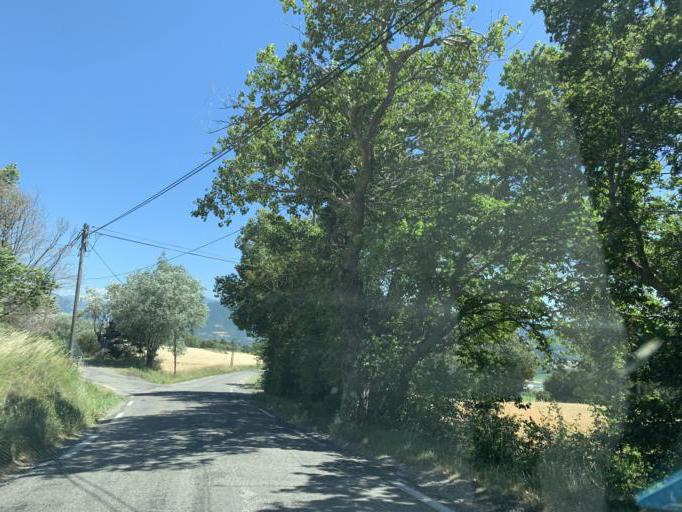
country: FR
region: Provence-Alpes-Cote d'Azur
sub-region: Departement des Hautes-Alpes
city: La Batie-Neuve
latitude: 44.5933
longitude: 6.1524
